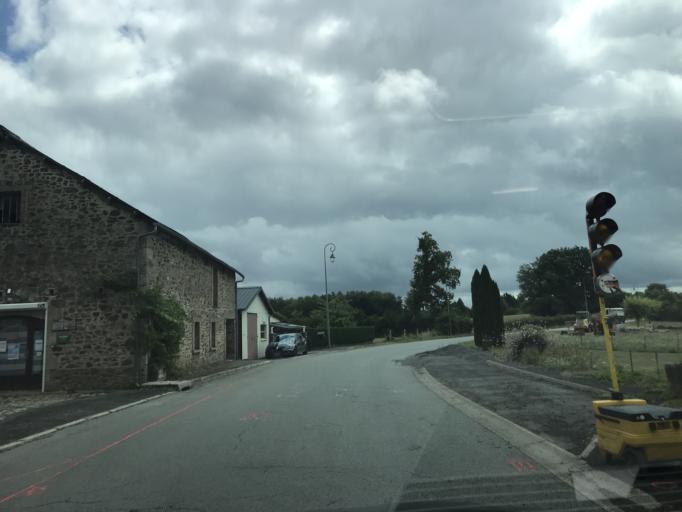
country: FR
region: Limousin
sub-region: Departement de la Correze
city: Neuvic
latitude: 45.2721
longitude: 2.2050
